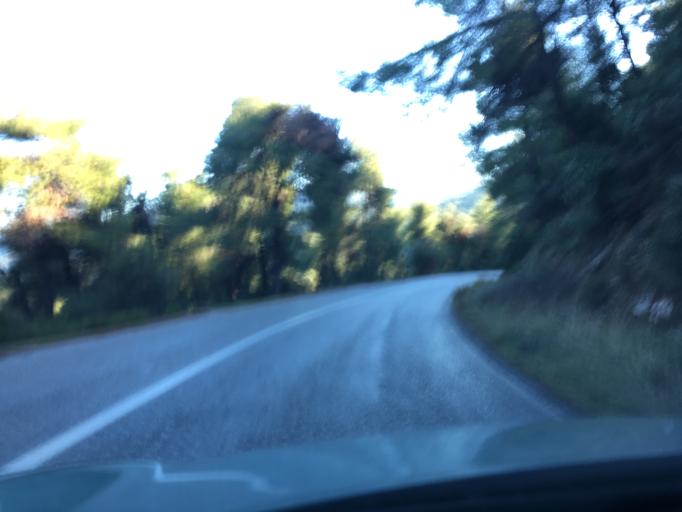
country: GR
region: Thessaly
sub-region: Nomos Magnisias
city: Skopelos
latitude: 39.0947
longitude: 23.7132
